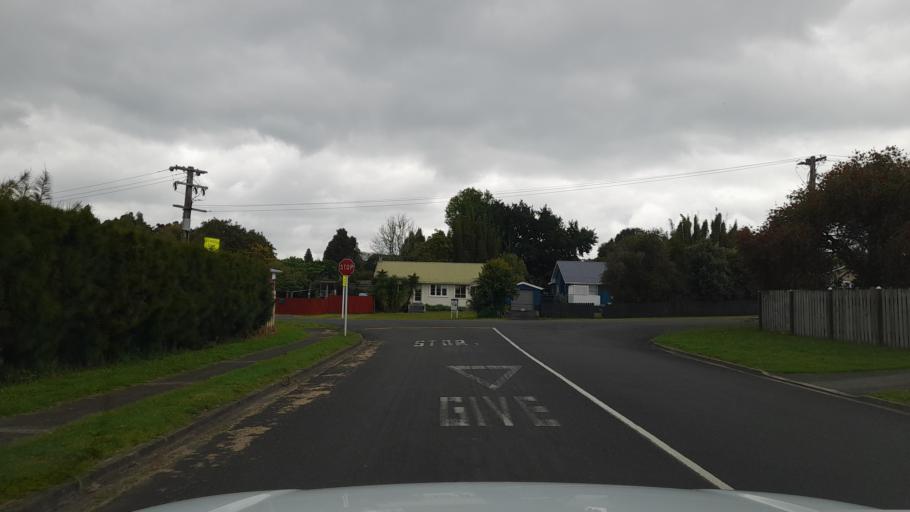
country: NZ
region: Northland
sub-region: Far North District
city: Waimate North
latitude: -35.4038
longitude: 173.7960
